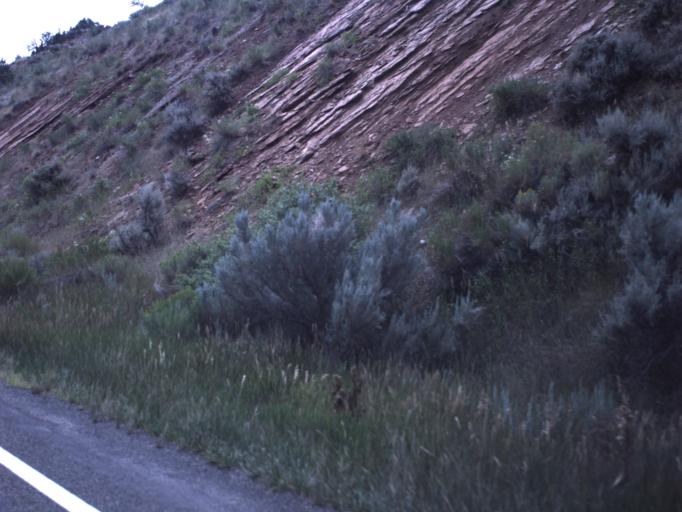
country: US
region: Utah
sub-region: Daggett County
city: Manila
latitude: 40.9259
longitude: -109.7161
